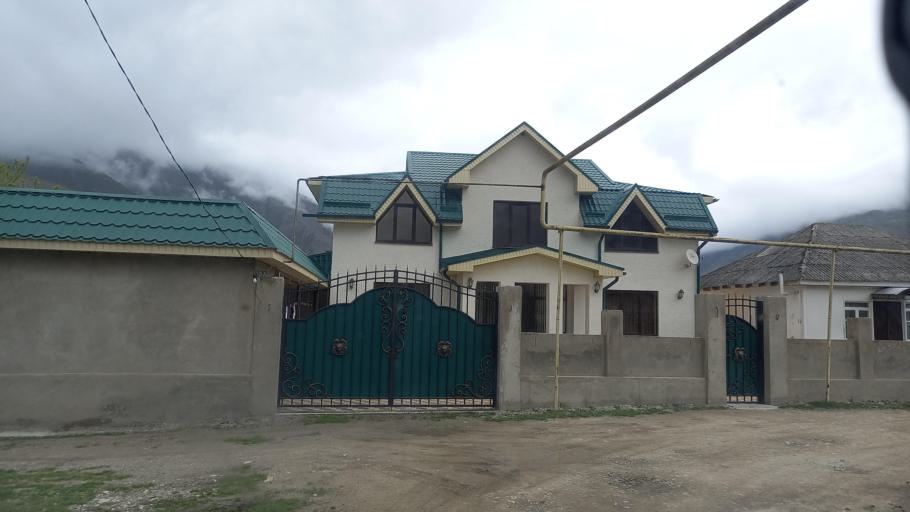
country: RU
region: Kabardino-Balkariya
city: Verkhnyaya Balkariya
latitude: 43.1171
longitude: 43.4396
